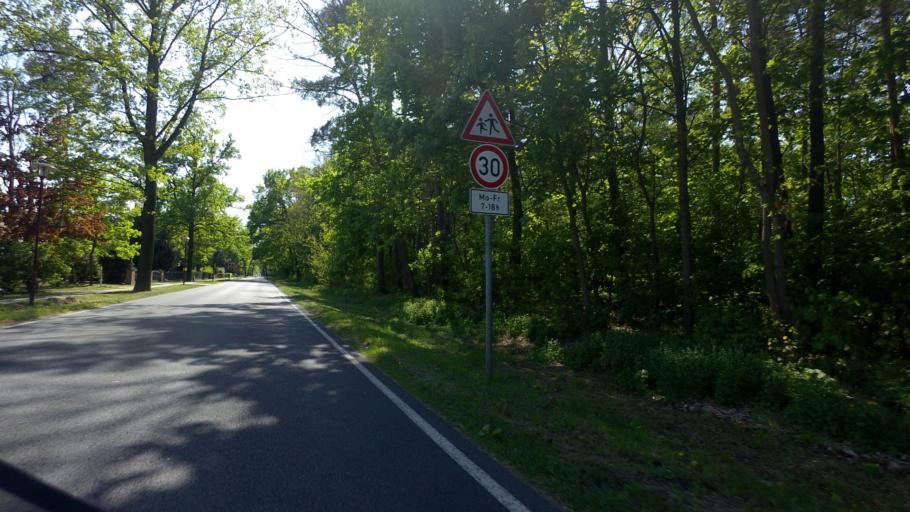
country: DE
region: Brandenburg
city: Tauche
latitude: 52.1141
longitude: 14.1893
